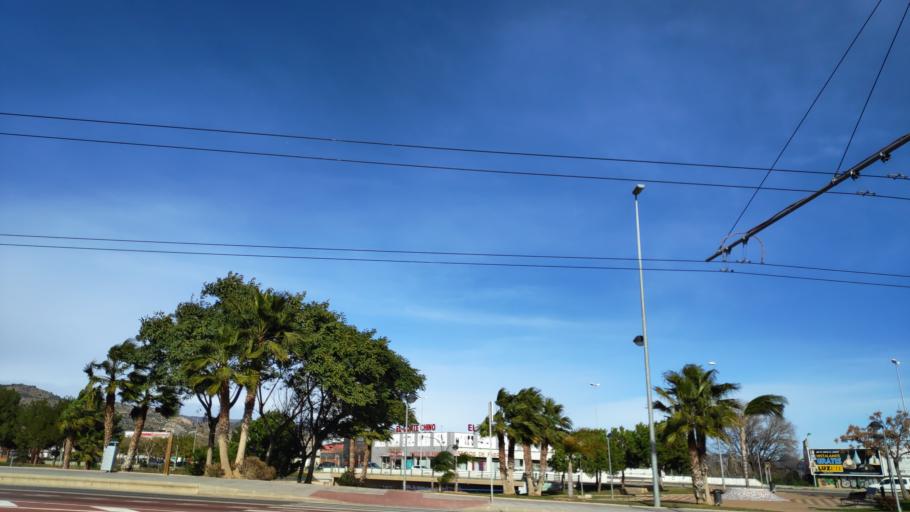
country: ES
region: Valencia
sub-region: Provincia de Castello
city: Castello de la Plana
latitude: 39.9905
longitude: -0.0549
